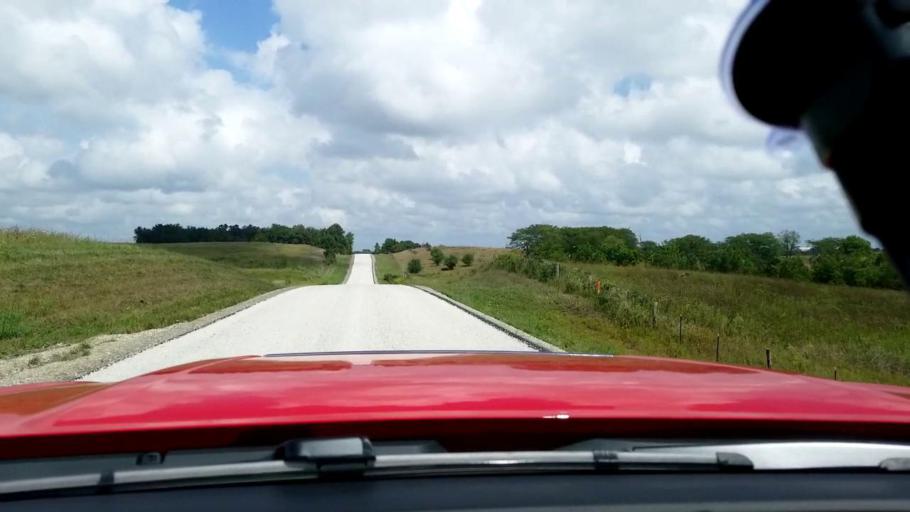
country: US
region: Iowa
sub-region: Decatur County
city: Lamoni
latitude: 40.6402
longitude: -94.0530
